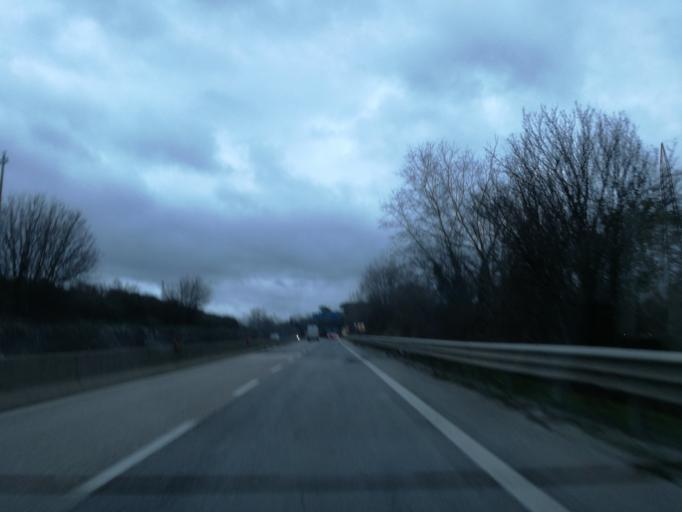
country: IT
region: Umbria
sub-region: Provincia di Perugia
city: Via Lippia
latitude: 43.0927
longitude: 12.4749
